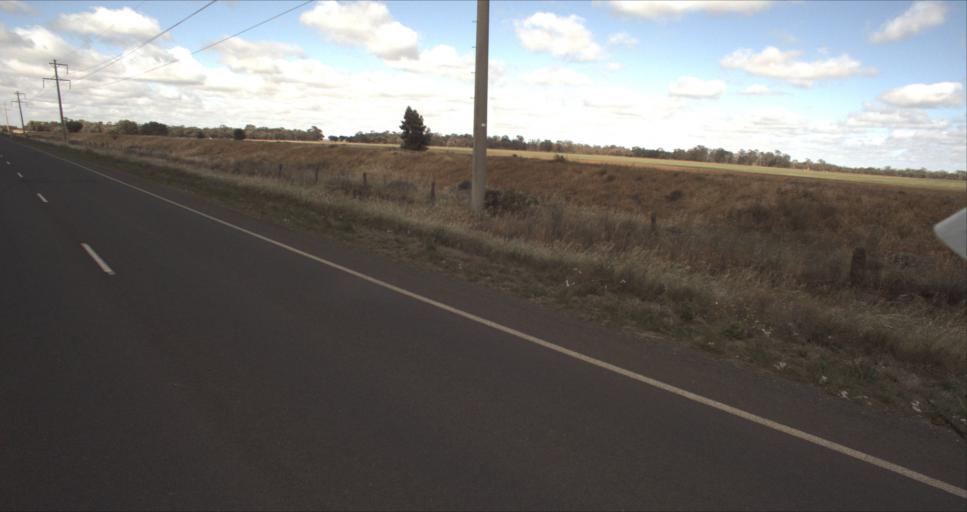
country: AU
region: New South Wales
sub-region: Murrumbidgee Shire
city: Darlington Point
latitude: -34.5365
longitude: 146.1730
